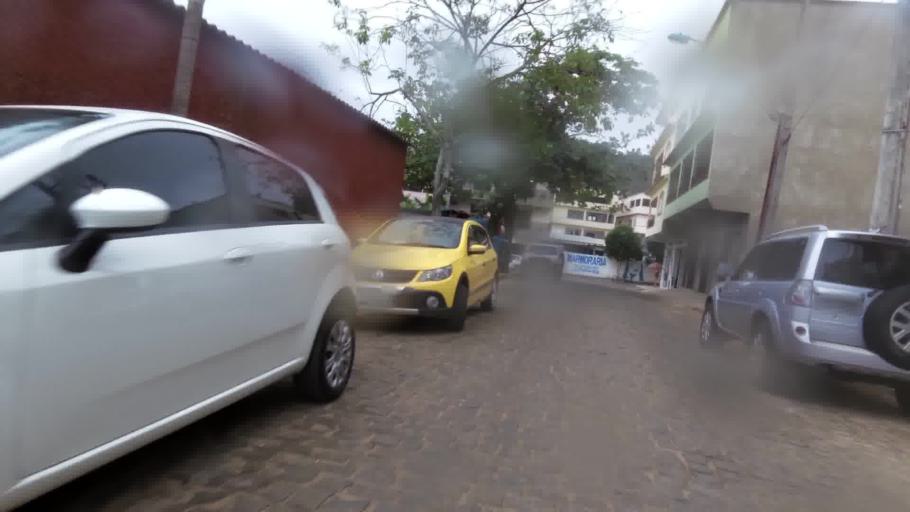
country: BR
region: Espirito Santo
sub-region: Alfredo Chaves
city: Alfredo Chaves
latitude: -20.6375
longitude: -40.7470
